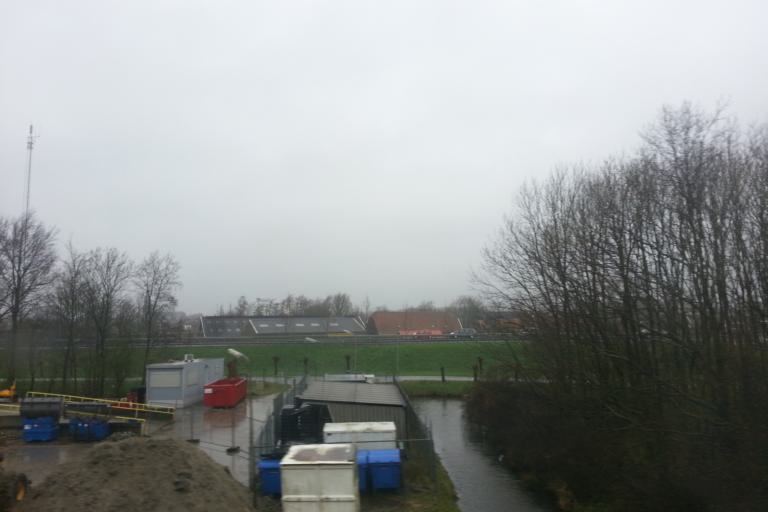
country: NL
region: South Holland
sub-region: Gemeente Teylingen
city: Sassenheim
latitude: 52.2175
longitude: 4.5279
